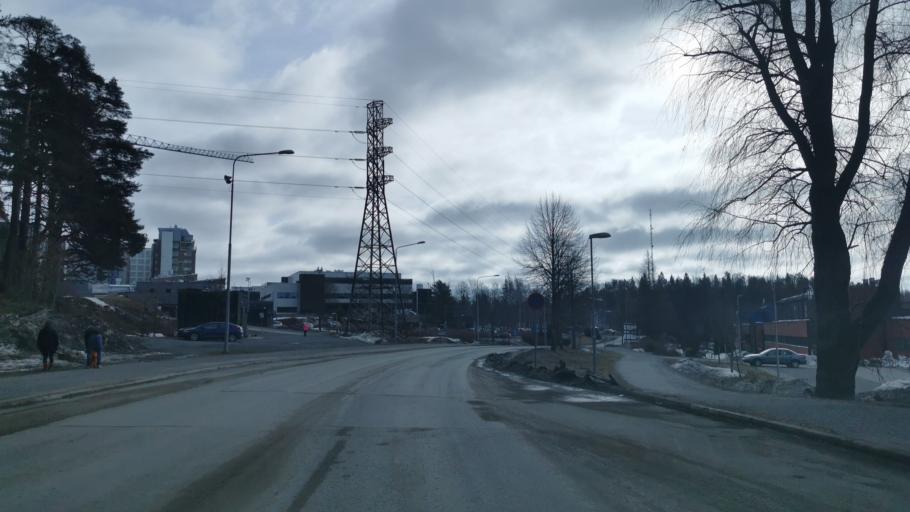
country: FI
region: Northern Savo
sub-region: Kuopio
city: Kuopio
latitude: 62.8975
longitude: 27.6397
